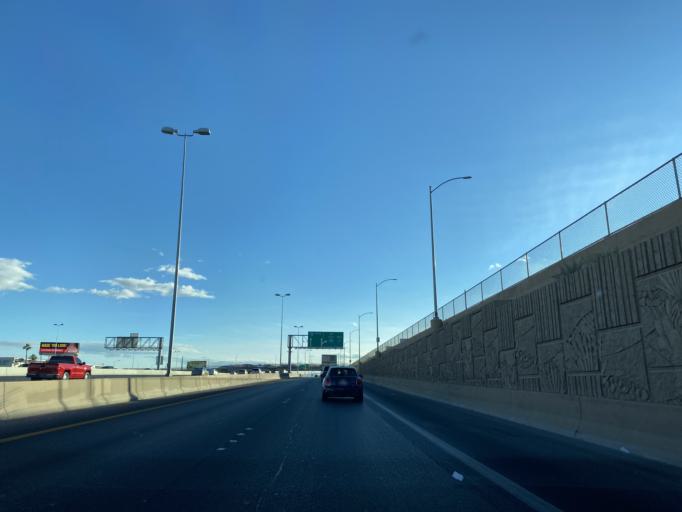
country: US
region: Nevada
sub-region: Clark County
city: Paradise
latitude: 36.0747
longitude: -115.1814
